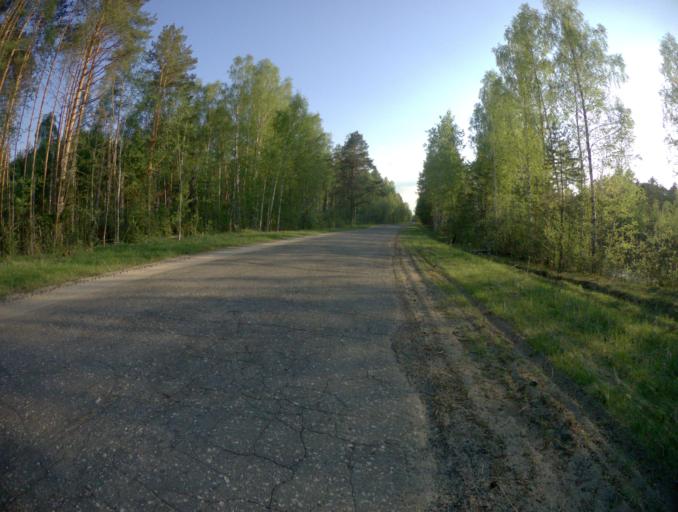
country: RU
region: Vladimir
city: Vyazniki
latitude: 56.3362
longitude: 42.1324
